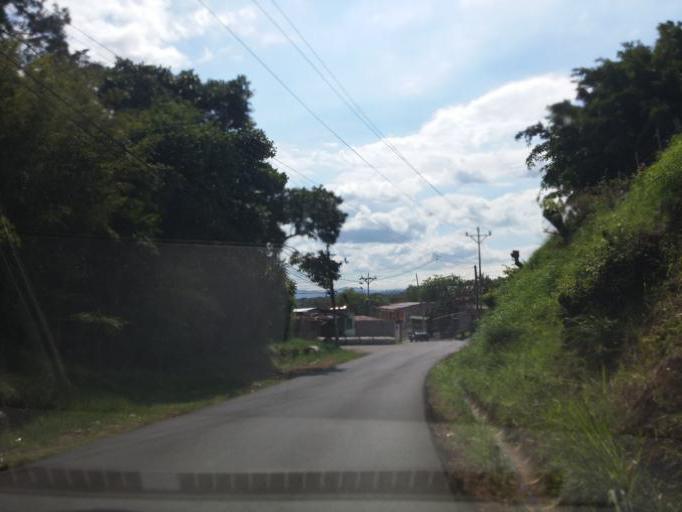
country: CR
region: Alajuela
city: Alajuela
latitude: 10.0194
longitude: -84.1840
